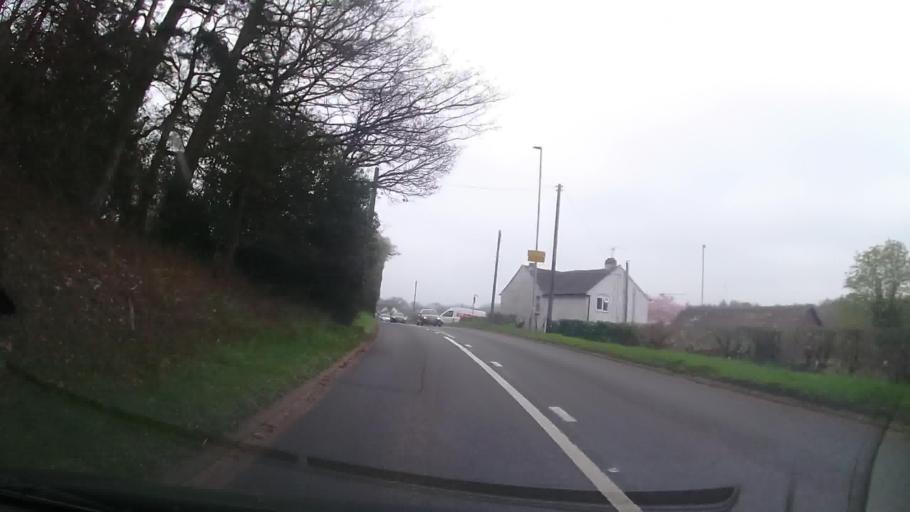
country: GB
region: England
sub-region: Staffordshire
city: Standon
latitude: 52.9465
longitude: -2.3438
